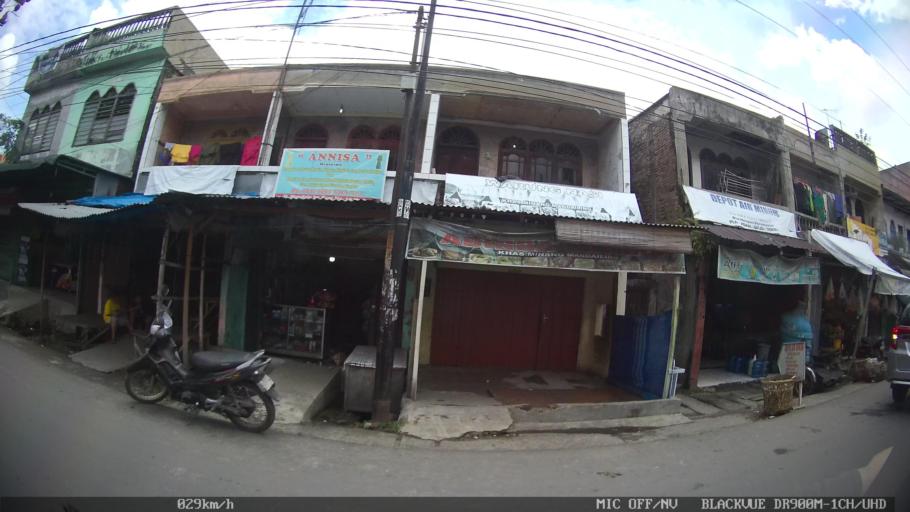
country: ID
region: North Sumatra
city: Medan
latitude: 3.5966
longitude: 98.7121
